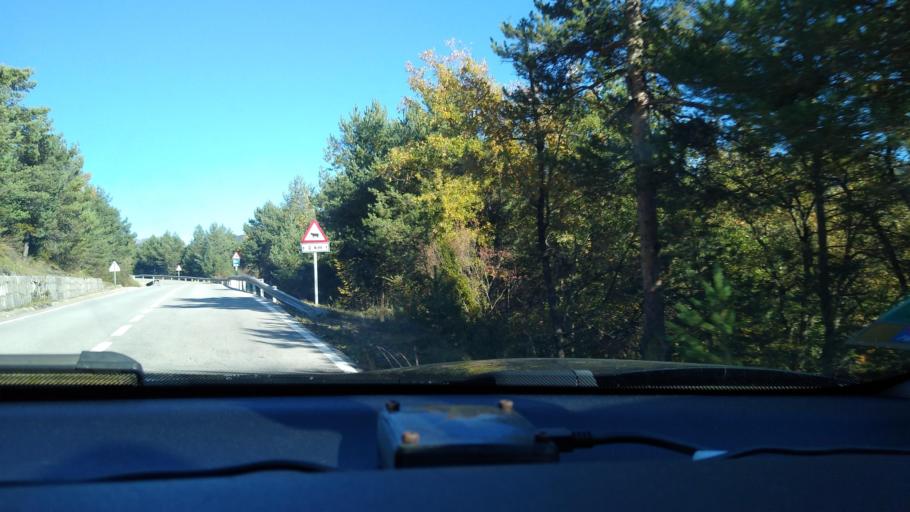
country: ES
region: Catalonia
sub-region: Provincia de Barcelona
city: Vallcebre
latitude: 42.2185
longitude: 1.8260
